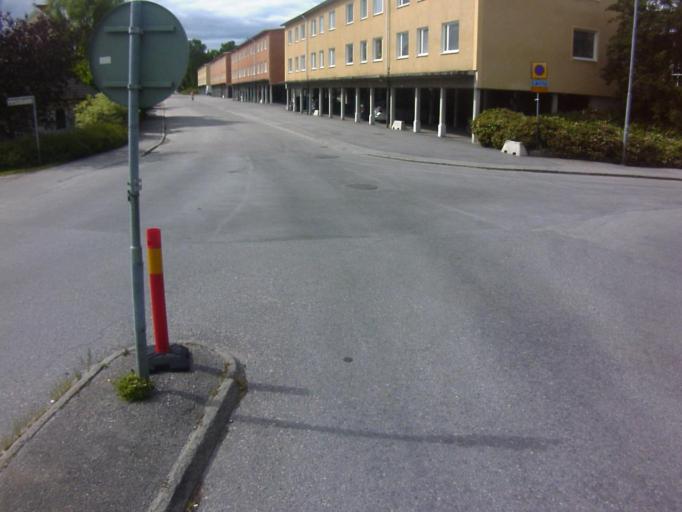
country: SE
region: Soedermanland
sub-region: Eskilstuna Kommun
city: Eskilstuna
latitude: 59.3686
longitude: 16.4992
